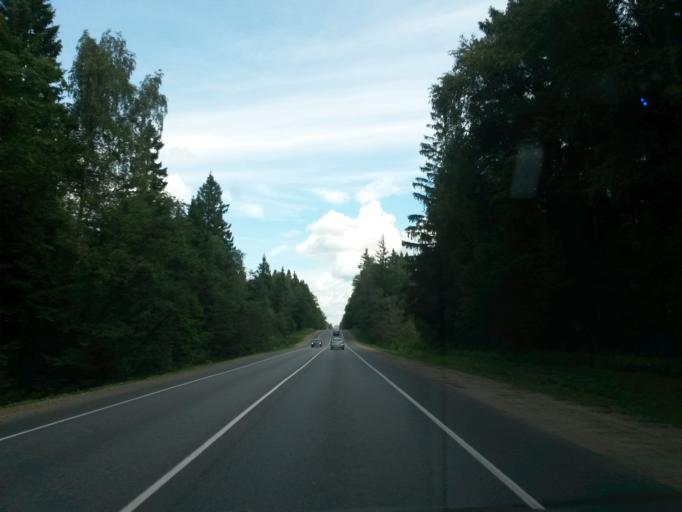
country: RU
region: Jaroslavl
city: Pereslavl'-Zalesskiy
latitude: 56.8041
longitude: 38.8955
